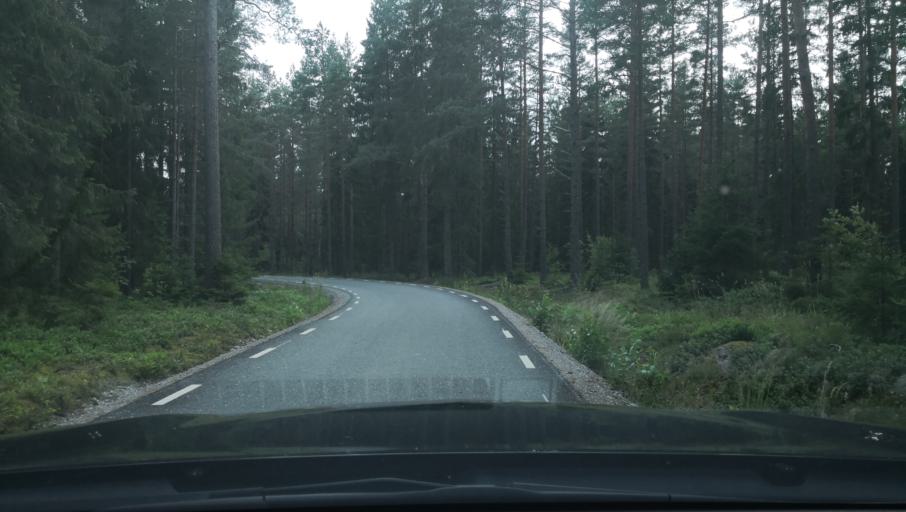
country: SE
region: Vaestmanland
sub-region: Surahammars Kommun
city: Surahammar
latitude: 59.6670
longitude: 16.1383
